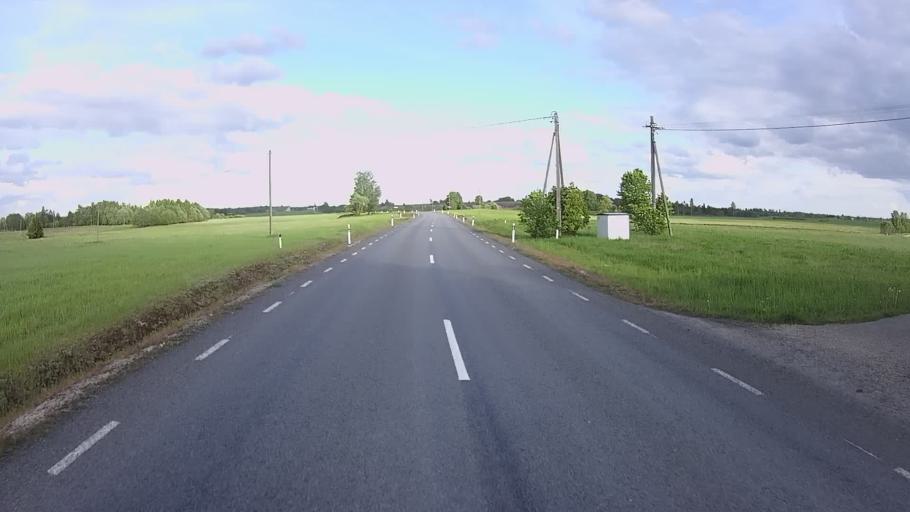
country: EE
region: Jogevamaa
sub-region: Mustvee linn
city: Mustvee
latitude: 59.0426
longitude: 27.0588
